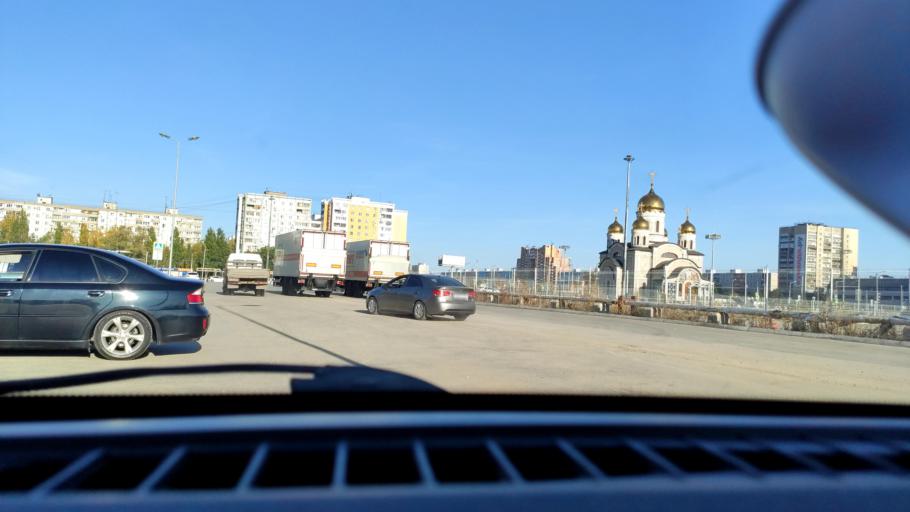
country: RU
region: Samara
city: Samara
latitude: 53.2511
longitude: 50.2190
